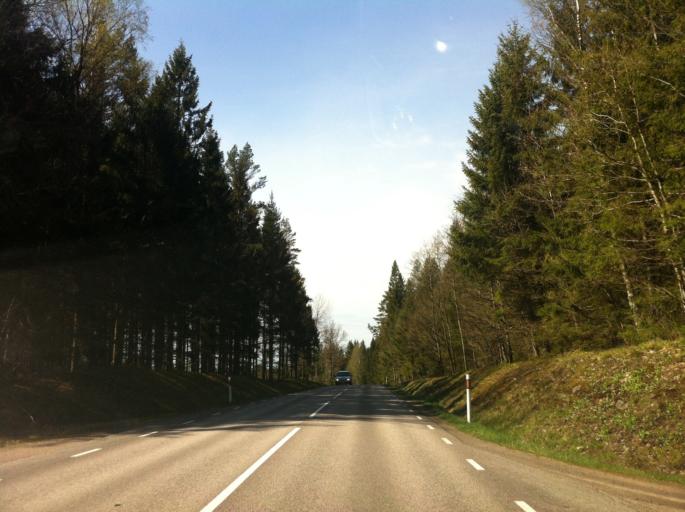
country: SE
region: Vaestra Goetaland
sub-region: Marks Kommun
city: Kinna
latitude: 57.1937
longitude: 12.8005
